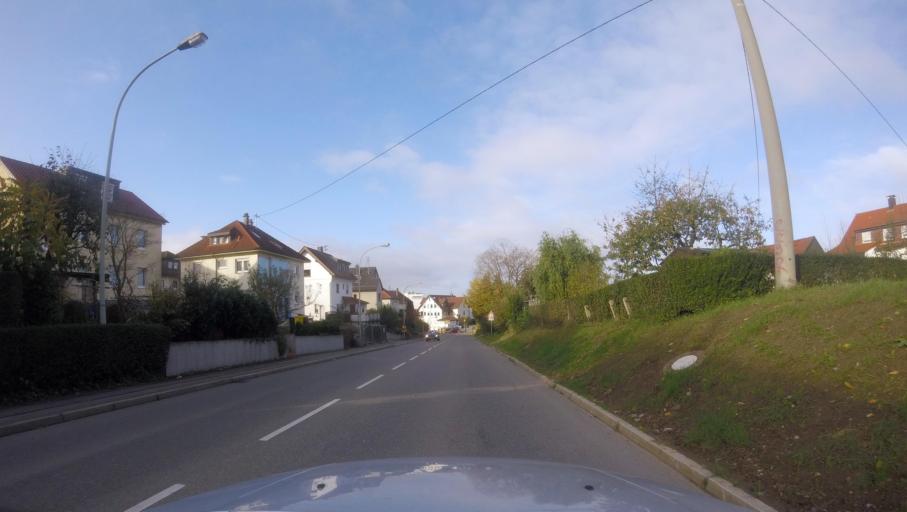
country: DE
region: Baden-Wuerttemberg
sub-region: Regierungsbezirk Stuttgart
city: Winnenden
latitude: 48.8798
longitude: 9.4032
